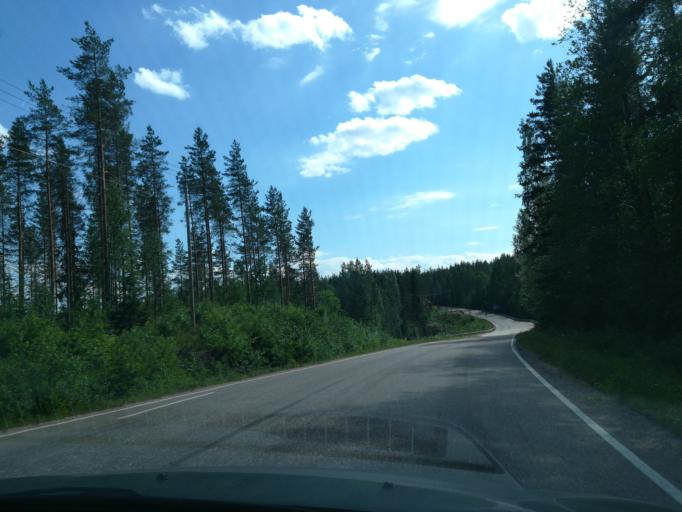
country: FI
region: South Karelia
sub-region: Imatra
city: Ruokolahti
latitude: 61.4795
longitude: 28.7891
